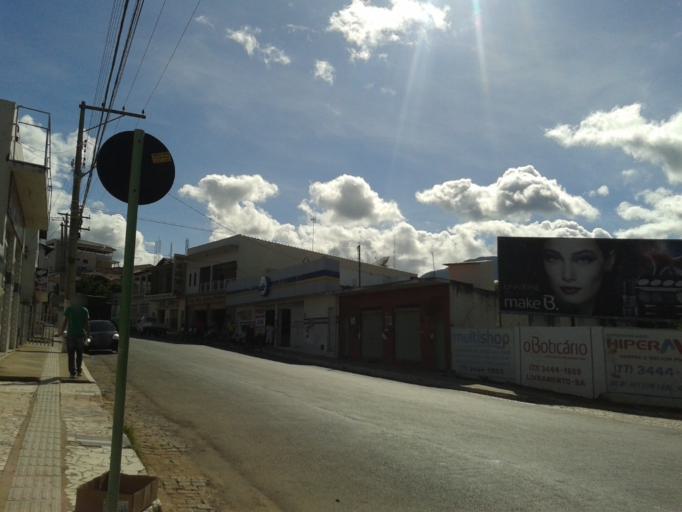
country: BR
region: Bahia
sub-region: Livramento Do Brumado
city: Livramento do Brumado
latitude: -13.6535
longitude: -41.8425
